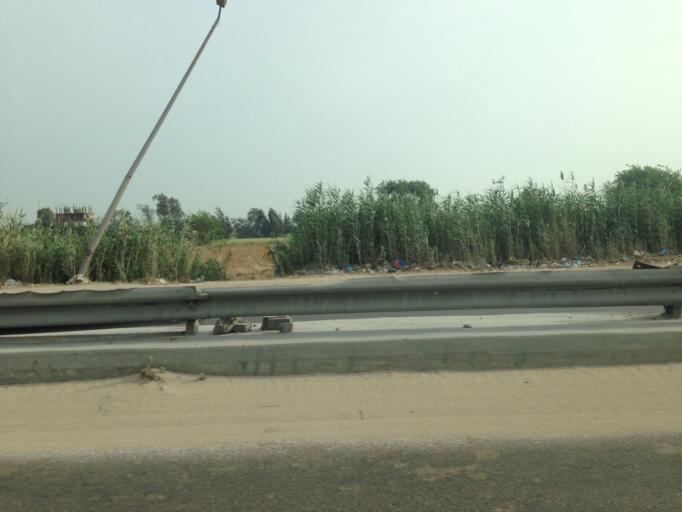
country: EG
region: Alexandria
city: Alexandria
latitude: 31.1973
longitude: 30.0303
